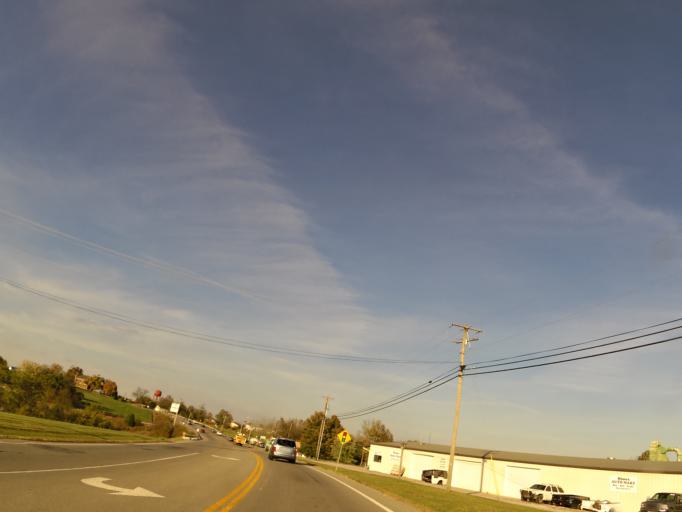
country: US
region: Kentucky
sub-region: Garrard County
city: Lancaster
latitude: 37.6052
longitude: -84.5813
